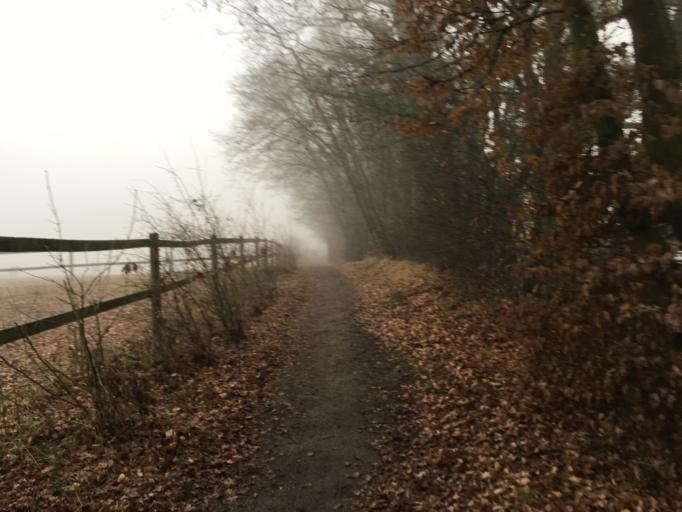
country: CH
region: Aargau
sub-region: Bezirk Zurzach
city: Koblenz
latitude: 47.6118
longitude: 8.2641
